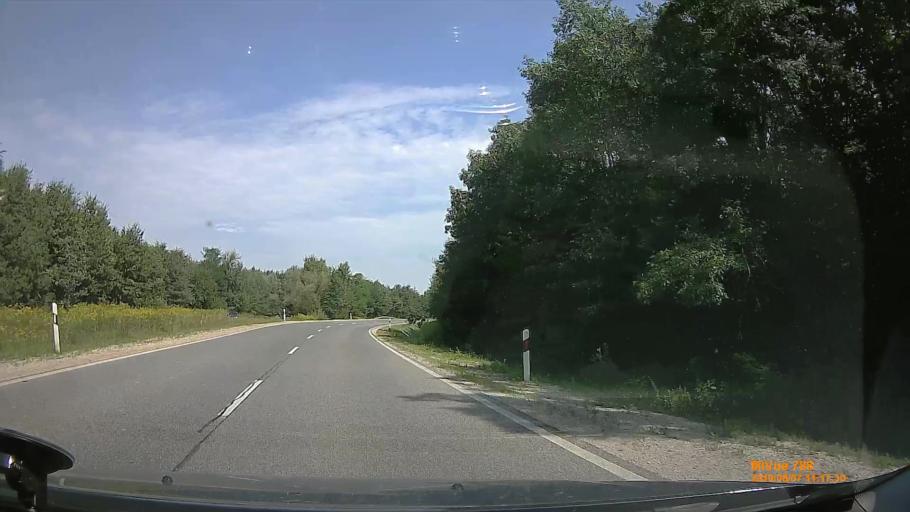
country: HU
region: Zala
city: Zalalovo
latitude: 46.7429
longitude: 16.5546
